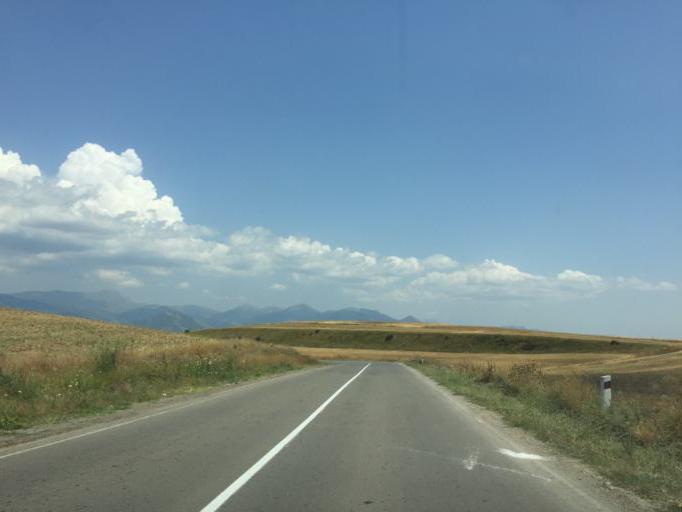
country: AM
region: Syunik'i Marz
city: Tegh
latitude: 39.5841
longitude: 46.5052
